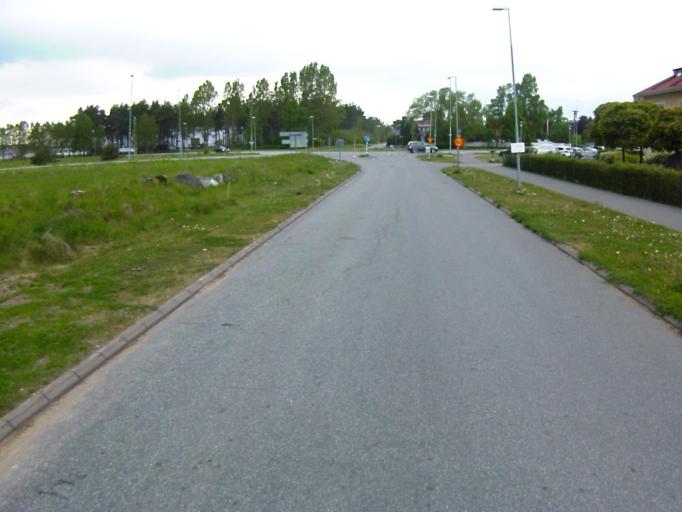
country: SE
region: Skane
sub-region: Kristianstads Kommun
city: Ahus
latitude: 55.9166
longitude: 14.2776
